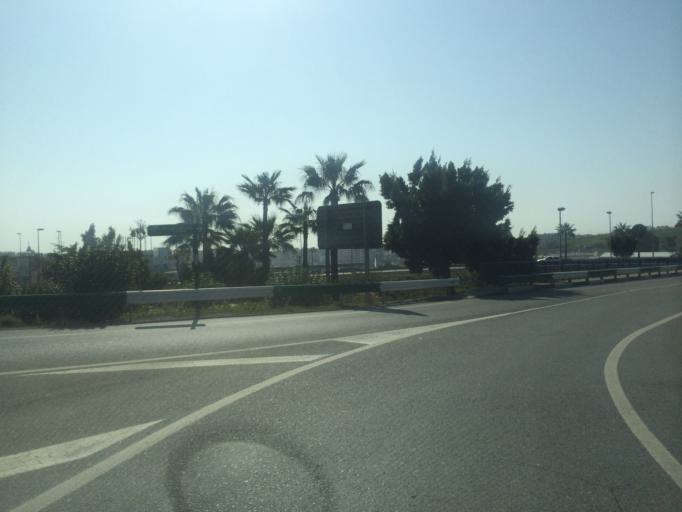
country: ES
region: Andalusia
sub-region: Provincia de Malaga
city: Estepona
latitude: 36.4338
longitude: -5.1615
